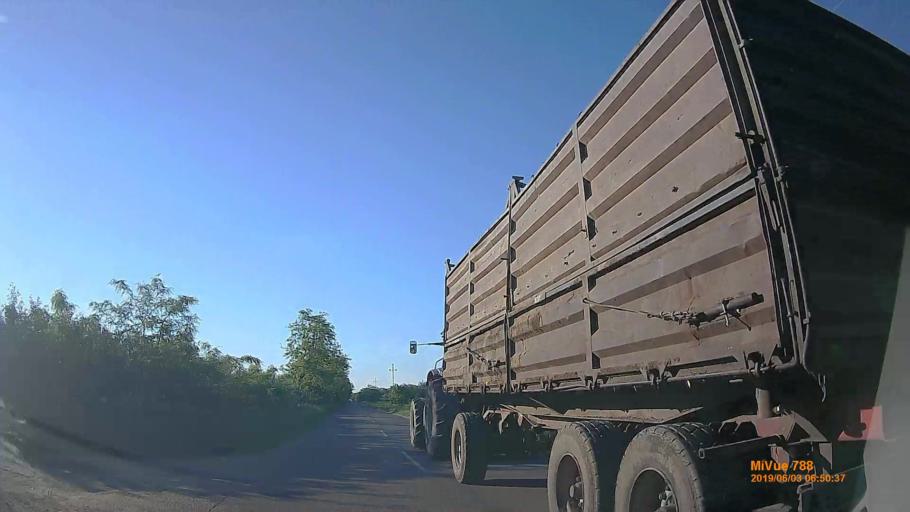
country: HU
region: Pest
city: Bugyi
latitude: 47.2185
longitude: 19.1744
